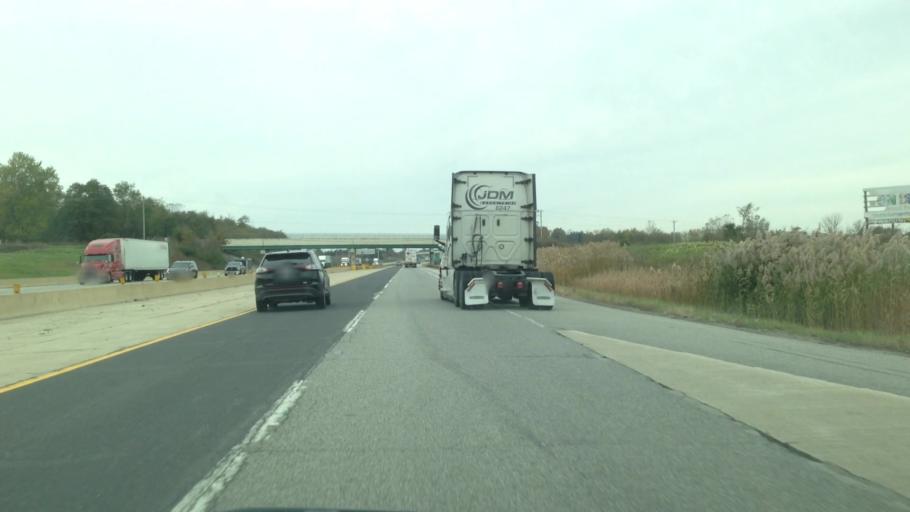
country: US
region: Indiana
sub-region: Steuben County
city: Fremont
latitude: 41.6675
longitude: -84.8560
